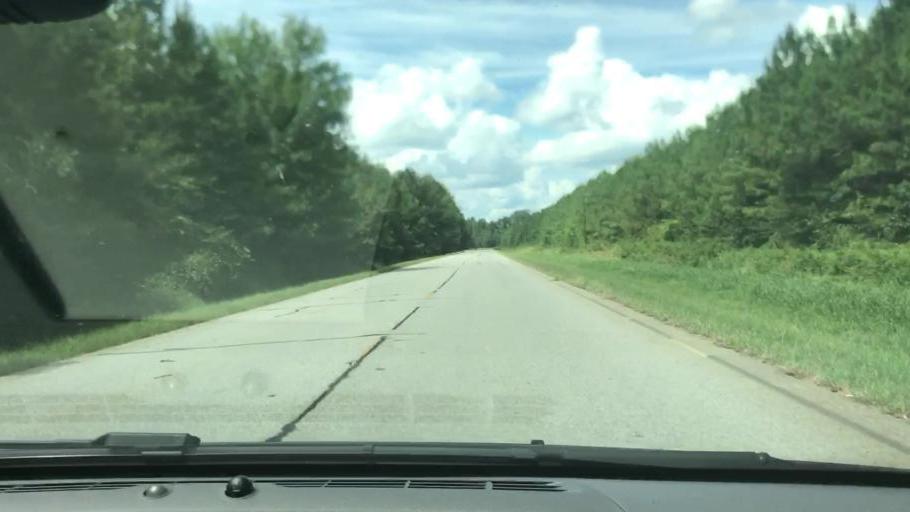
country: US
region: Georgia
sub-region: Stewart County
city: Lumpkin
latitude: 32.1441
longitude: -84.8822
